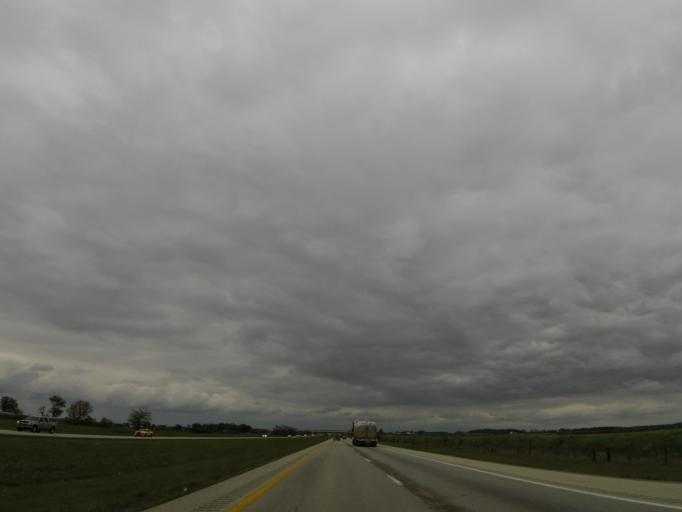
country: US
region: Ohio
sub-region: Greene County
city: Shawnee Hills
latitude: 39.5442
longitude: -83.7580
